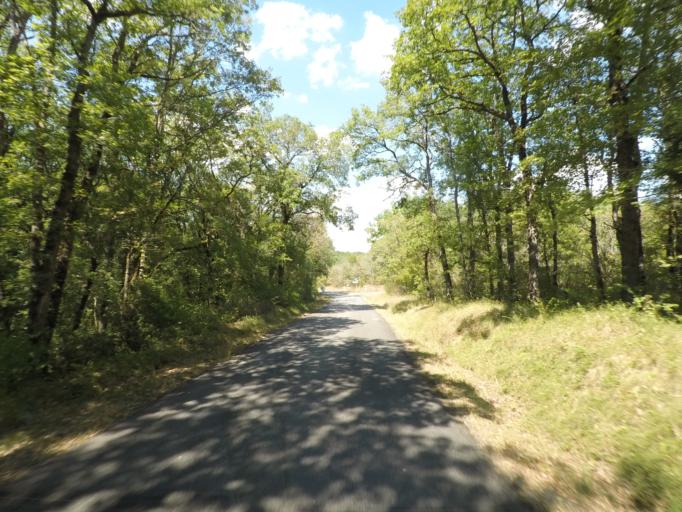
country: FR
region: Midi-Pyrenees
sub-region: Departement du Lot
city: Cahors
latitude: 44.5484
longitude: 1.5933
